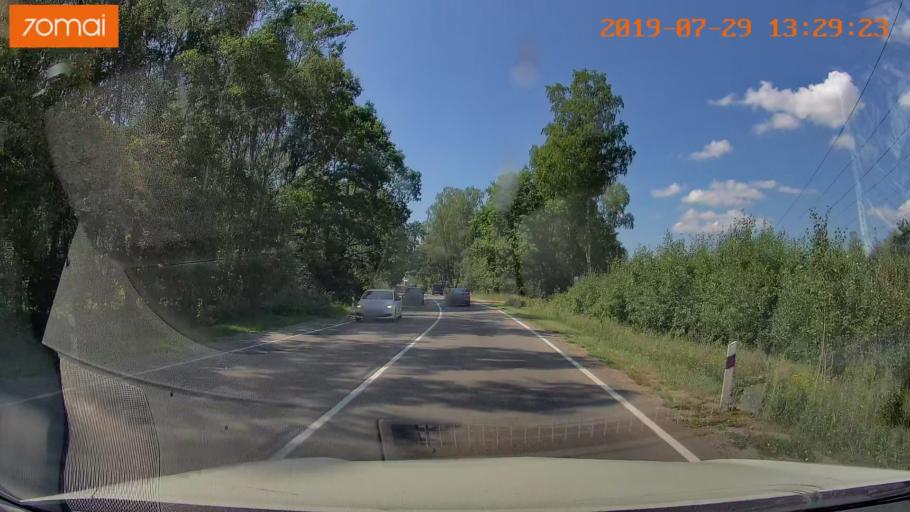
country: RU
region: Kaliningrad
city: Vzmorye
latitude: 54.7027
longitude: 20.2691
